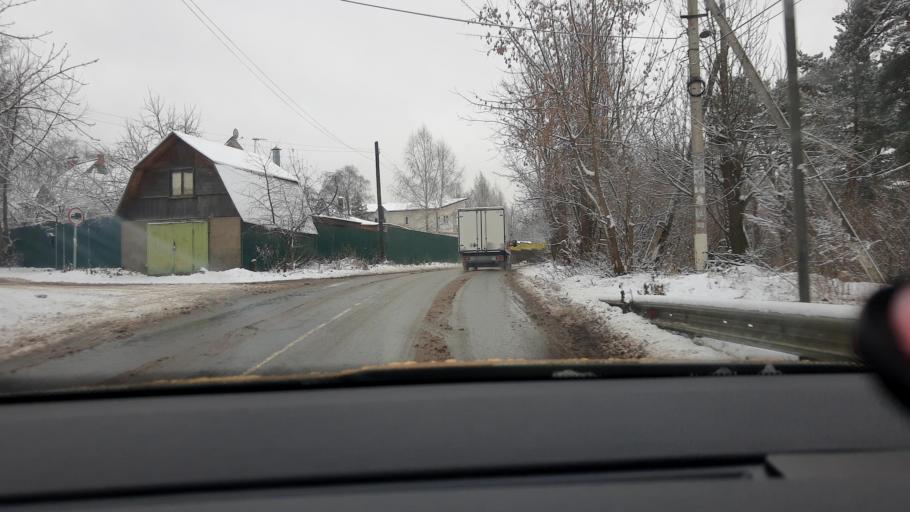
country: RU
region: Moskovskaya
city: Mamontovka
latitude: 55.9716
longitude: 37.8262
